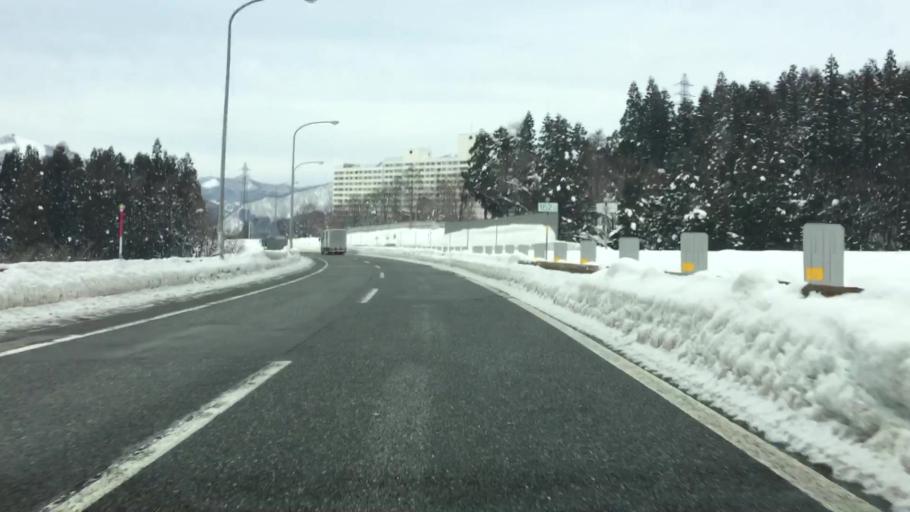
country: JP
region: Niigata
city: Shiozawa
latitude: 36.9009
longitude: 138.8474
